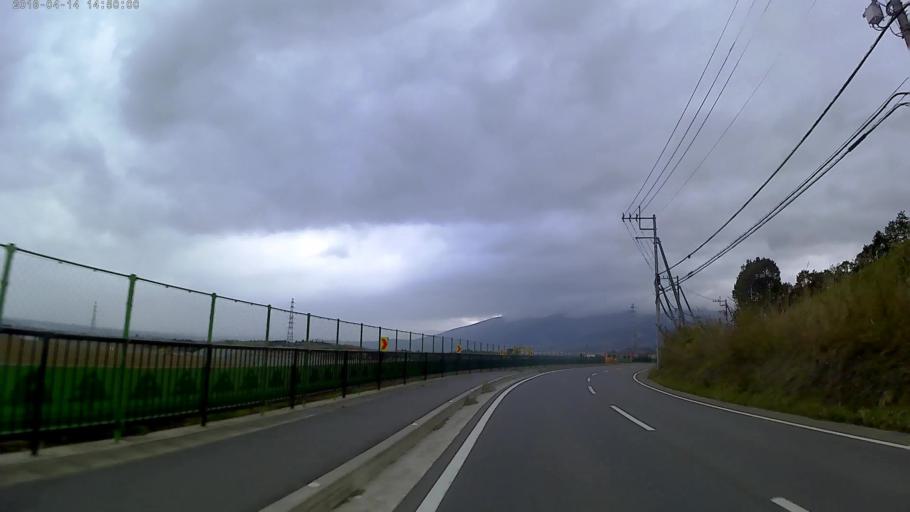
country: JP
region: Shizuoka
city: Gotemba
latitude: 35.3629
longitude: 138.9698
